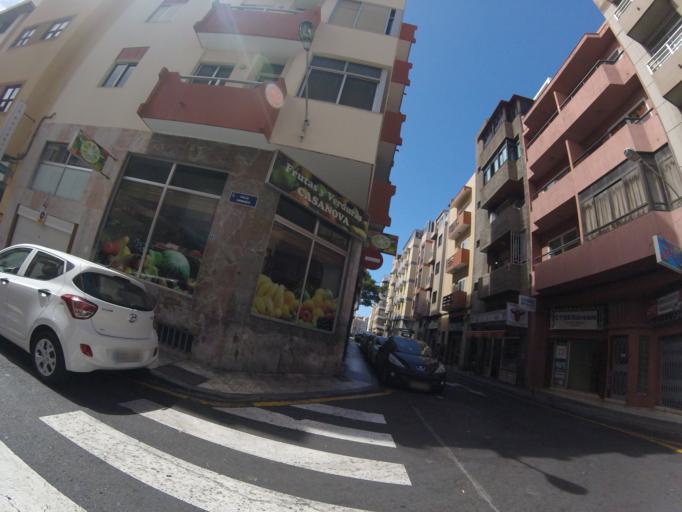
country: ES
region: Canary Islands
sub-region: Provincia de Santa Cruz de Tenerife
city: Santa Cruz de Tenerife
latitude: 28.4669
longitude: -16.2569
